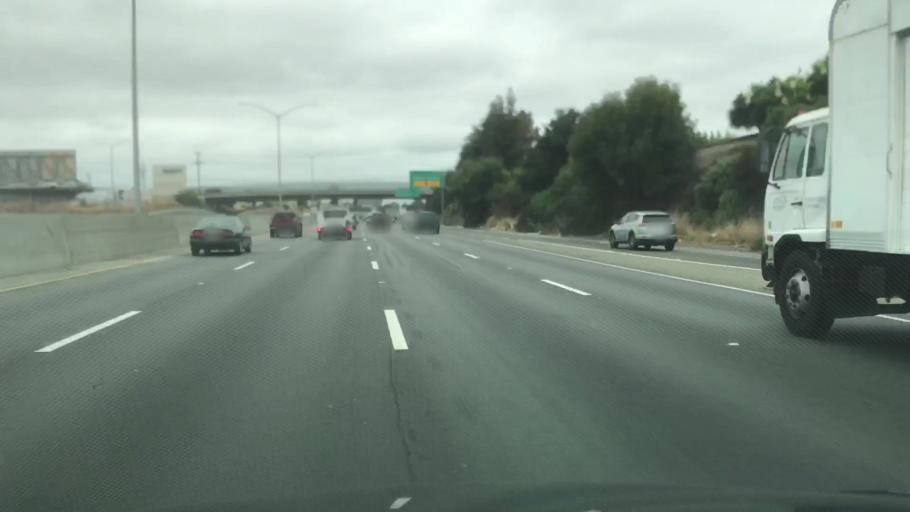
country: US
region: California
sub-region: Alameda County
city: San Leandro
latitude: 37.7110
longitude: -122.1663
